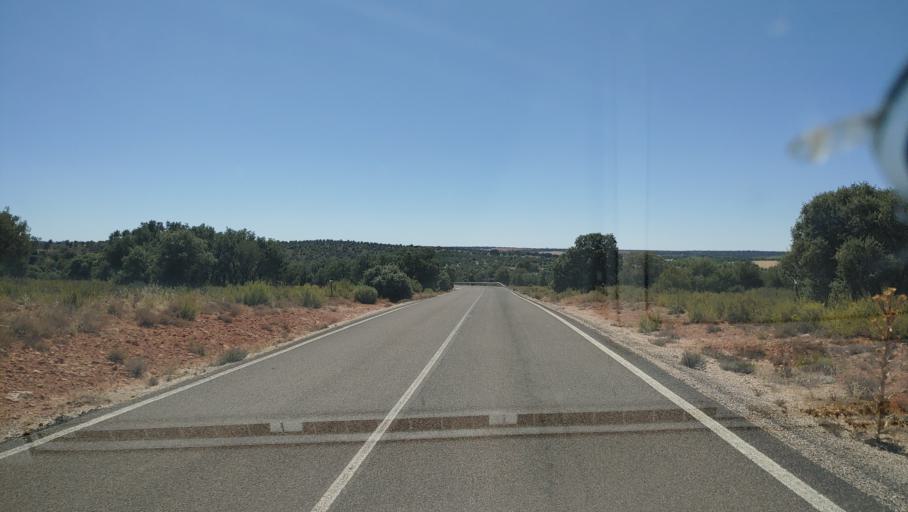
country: ES
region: Castille-La Mancha
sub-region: Provincia de Albacete
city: Ossa de Montiel
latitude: 38.8776
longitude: -2.7843
